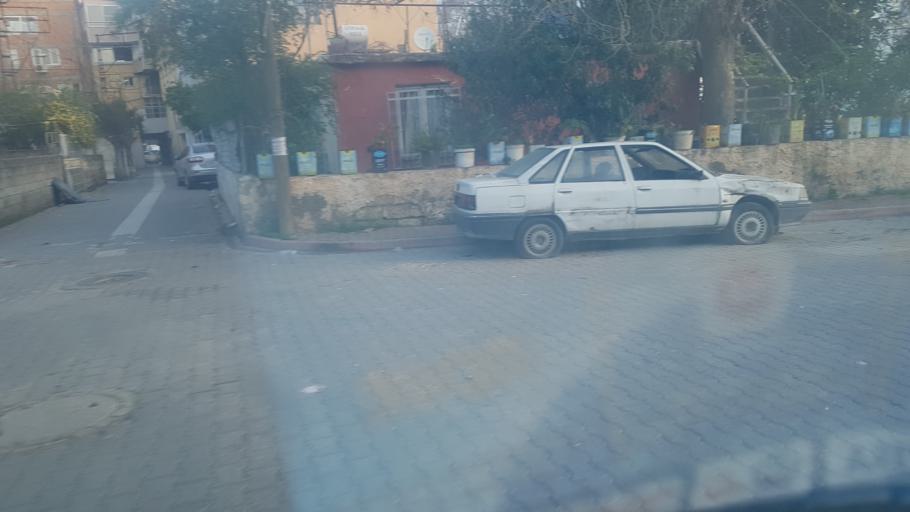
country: TR
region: Adana
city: Adana
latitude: 37.0110
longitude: 35.3297
